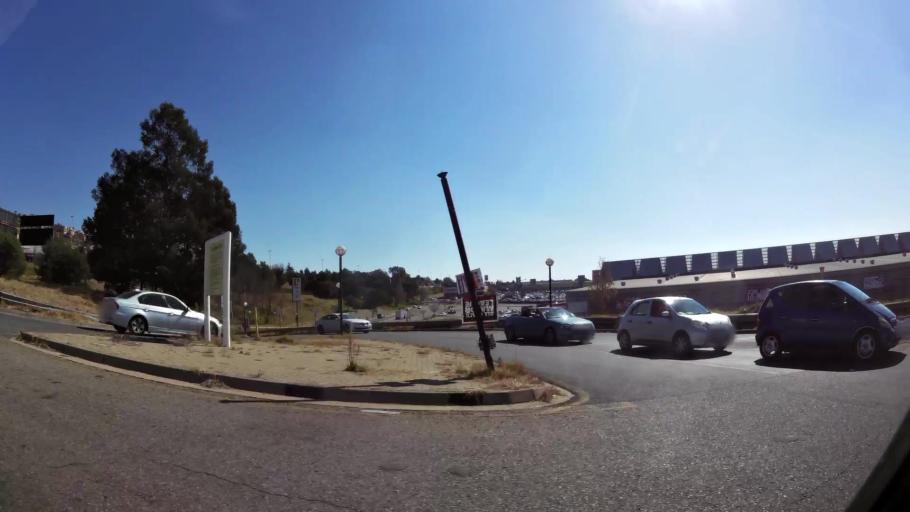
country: ZA
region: Gauteng
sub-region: City of Johannesburg Metropolitan Municipality
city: Roodepoort
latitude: -26.1436
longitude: 27.9228
